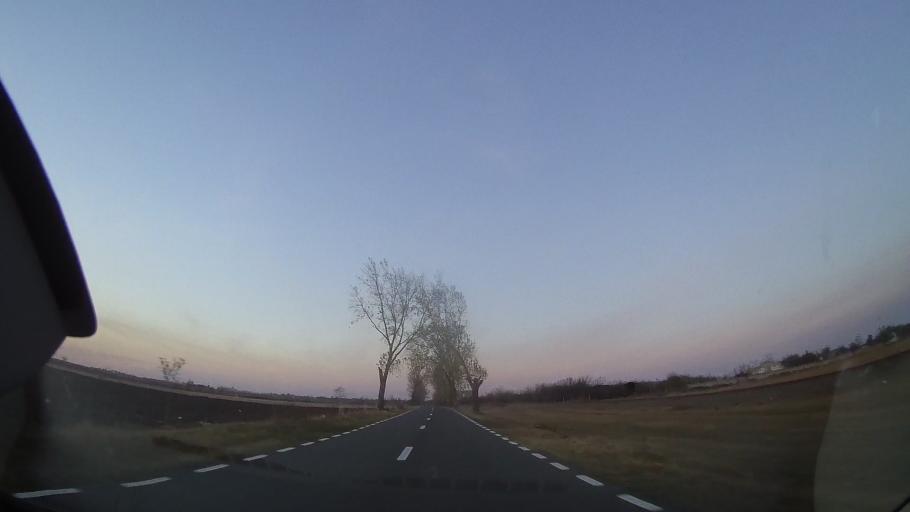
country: RO
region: Constanta
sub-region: Comuna Cobadin
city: Cobadin
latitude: 44.0434
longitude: 28.2546
